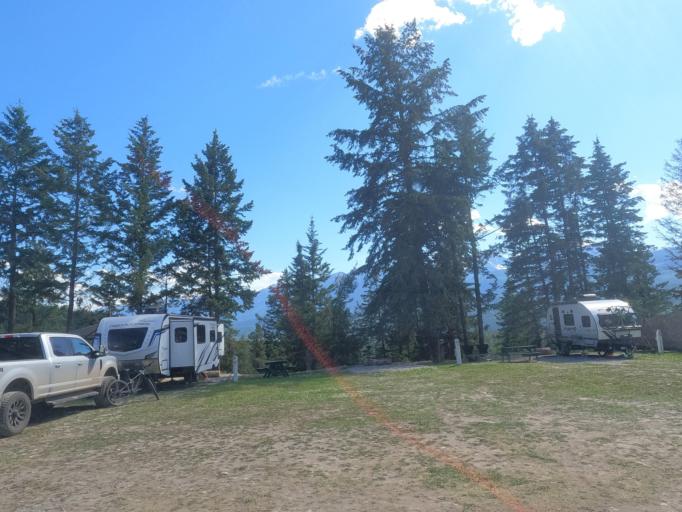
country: CA
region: British Columbia
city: Golden
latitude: 51.3003
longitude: -116.9478
